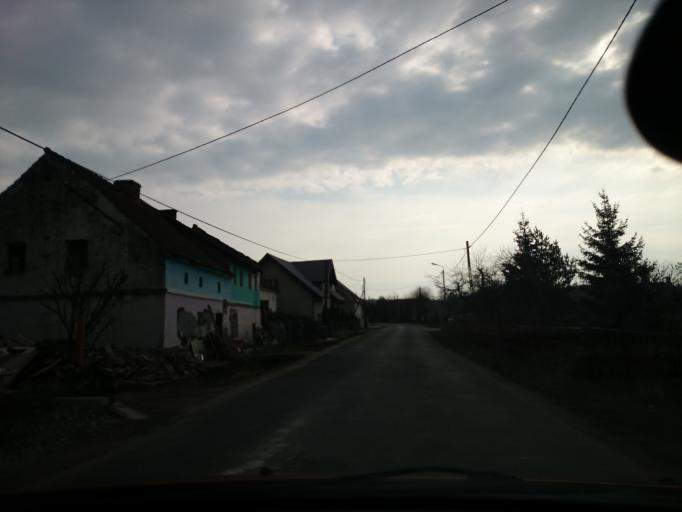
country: PL
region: Lower Silesian Voivodeship
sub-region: Powiat zabkowicki
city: Kamieniec Zabkowicki
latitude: 50.5260
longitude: 16.8642
